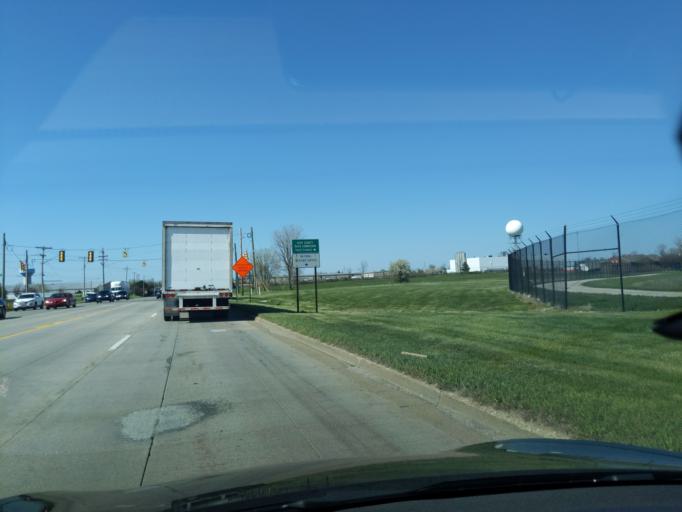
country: US
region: Michigan
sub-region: Kent County
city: East Grand Rapids
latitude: 42.8908
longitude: -85.5475
